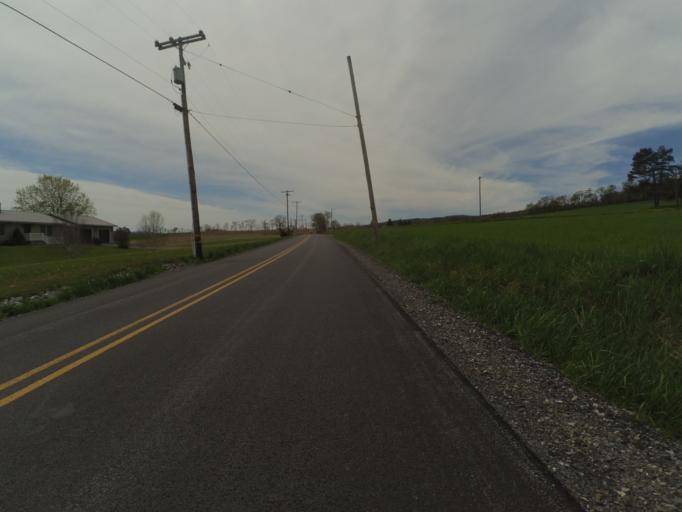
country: US
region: Pennsylvania
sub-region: Blair County
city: Tyrone
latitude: 40.6964
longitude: -78.1766
